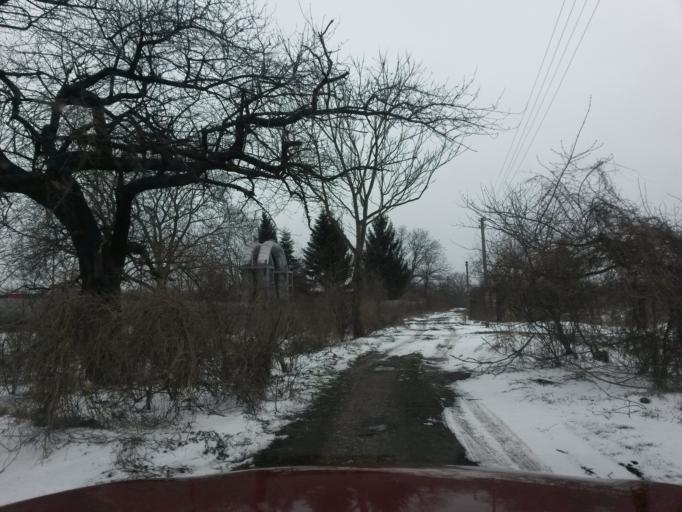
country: SK
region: Kosicky
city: Kosice
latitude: 48.7017
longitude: 21.2691
